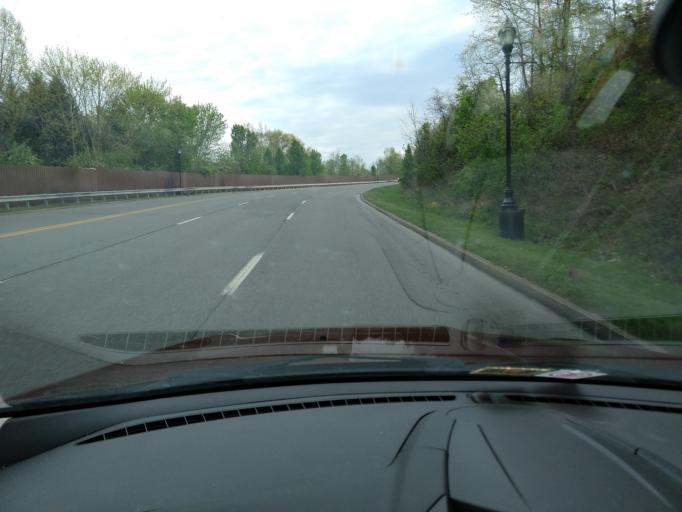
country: US
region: West Virginia
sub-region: Harrison County
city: Bridgeport
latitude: 39.3115
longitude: -80.2768
